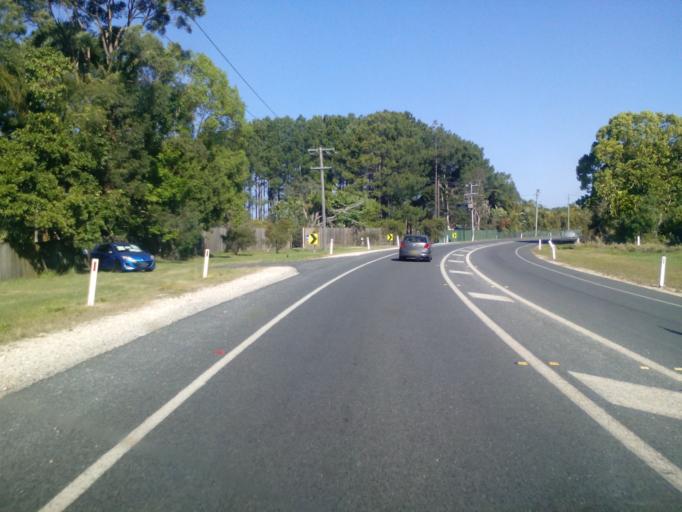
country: AU
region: New South Wales
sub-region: Tweed
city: Kingscliff
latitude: -28.2524
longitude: 153.5589
